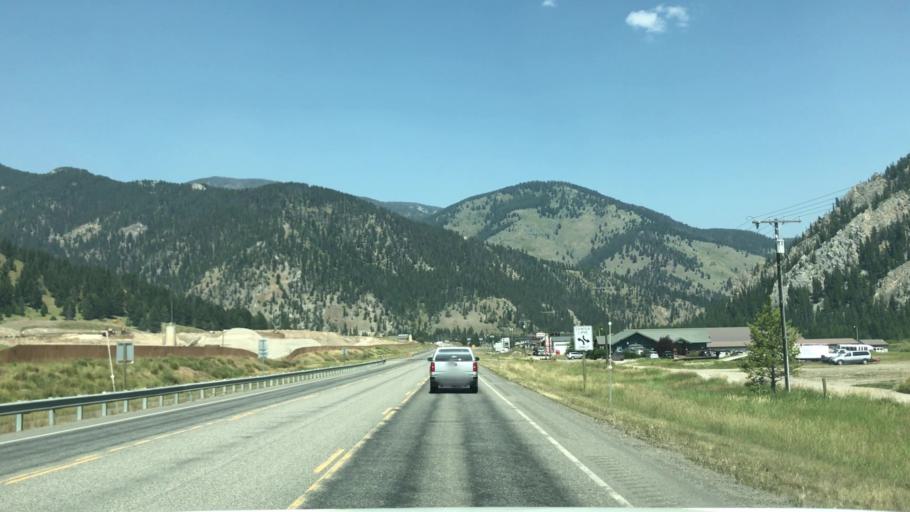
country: US
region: Montana
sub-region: Gallatin County
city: Big Sky
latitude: 45.2552
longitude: -111.2544
